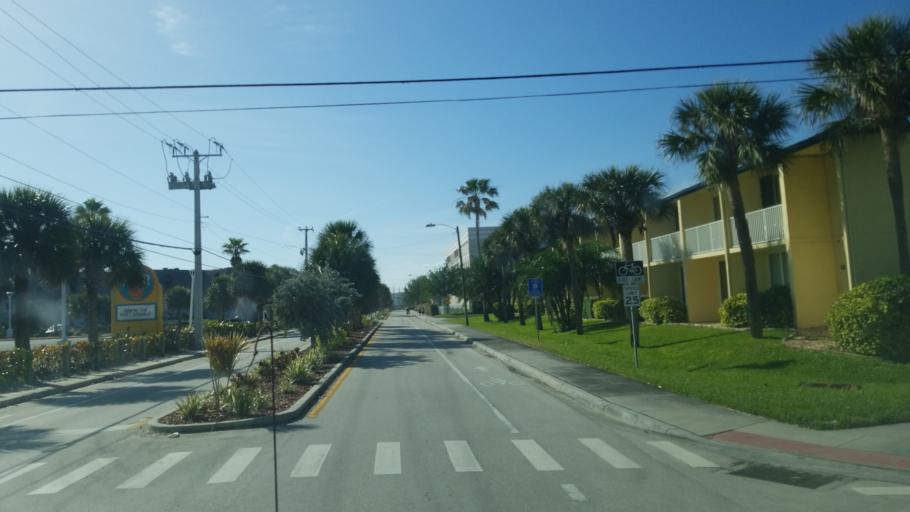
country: US
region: Florida
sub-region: Brevard County
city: Cape Canaveral
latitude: 28.3680
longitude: -80.6043
